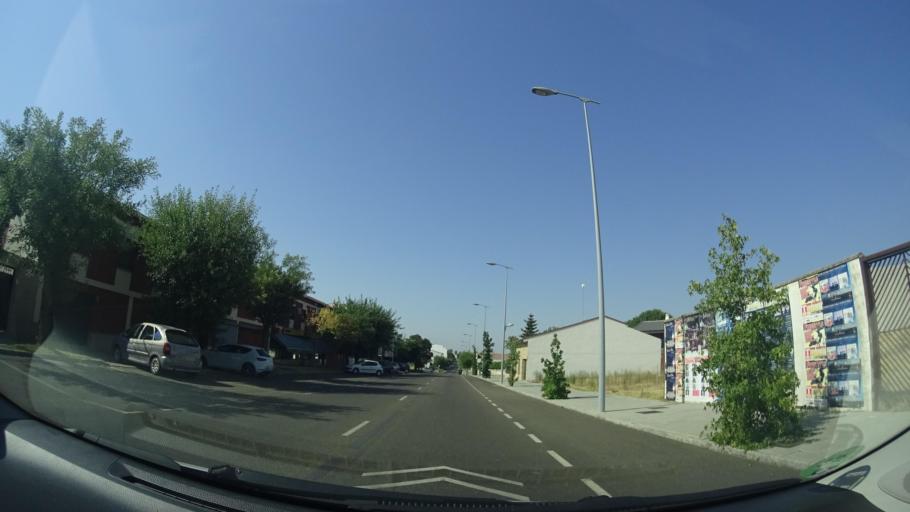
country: ES
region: Extremadura
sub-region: Provincia de Caceres
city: Miajadas
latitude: 39.1590
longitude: -5.8992
